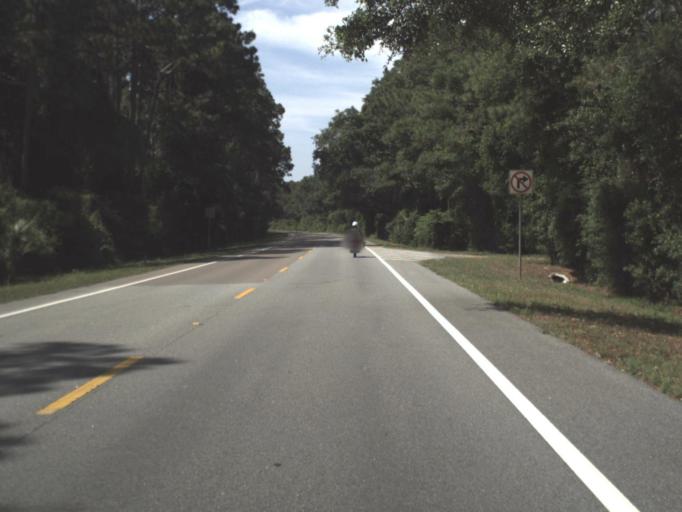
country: US
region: Florida
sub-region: Duval County
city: Atlantic Beach
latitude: 30.4821
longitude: -81.4393
